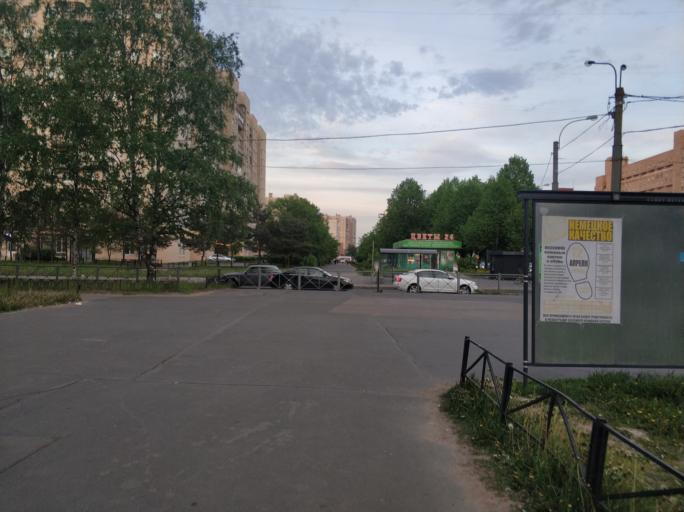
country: RU
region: St.-Petersburg
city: Komendantsky aerodrom
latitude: 59.9994
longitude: 30.2820
